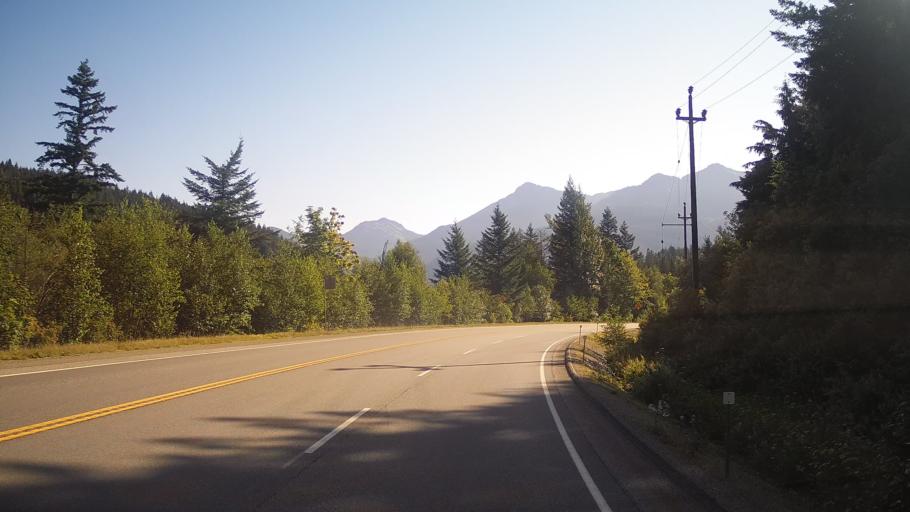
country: CA
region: British Columbia
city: Hope
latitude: 49.4081
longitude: -121.4521
